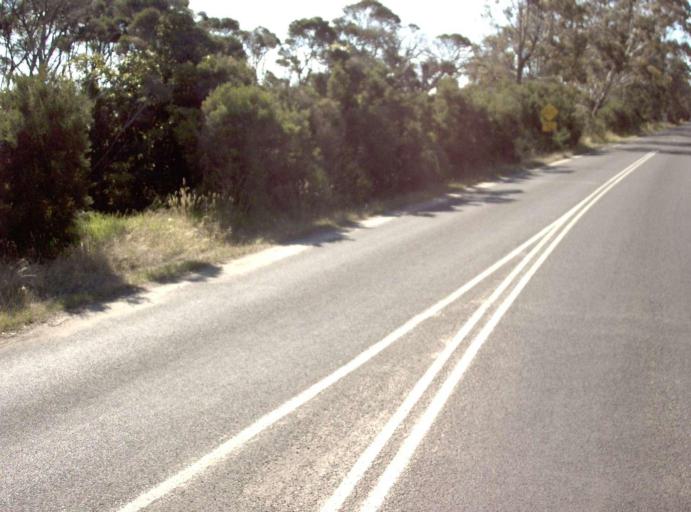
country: AU
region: Victoria
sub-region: Latrobe
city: Traralgon
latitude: -38.6650
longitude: 146.6879
